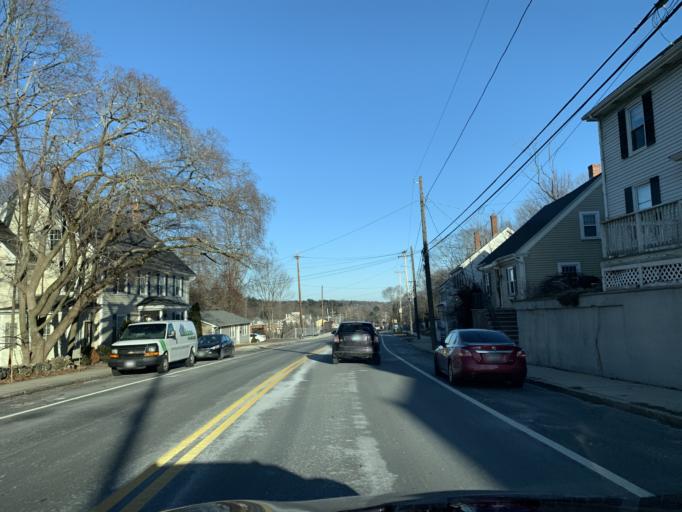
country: US
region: Massachusetts
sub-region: Essex County
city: Andover
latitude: 42.6595
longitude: -71.1430
